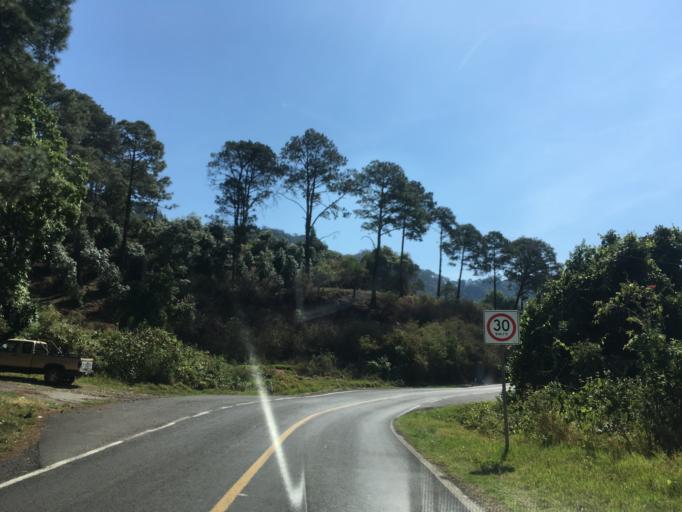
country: MX
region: Michoacan
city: Tzitzio
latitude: 19.6497
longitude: -100.9837
